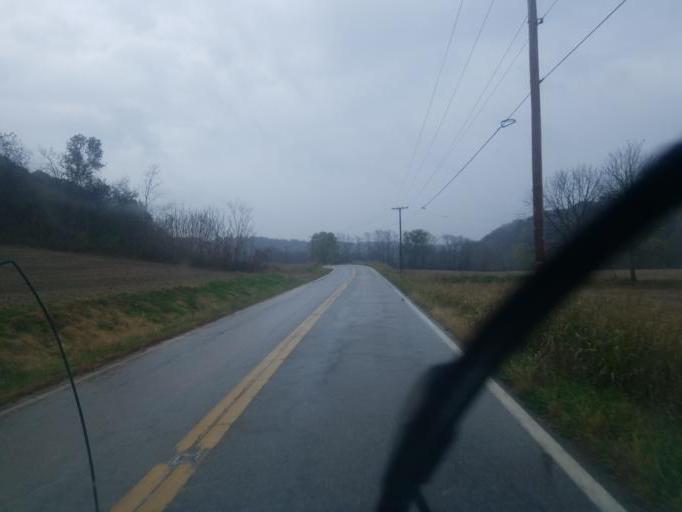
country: US
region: Ohio
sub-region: Morgan County
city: McConnelsville
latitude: 39.5740
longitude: -81.7840
